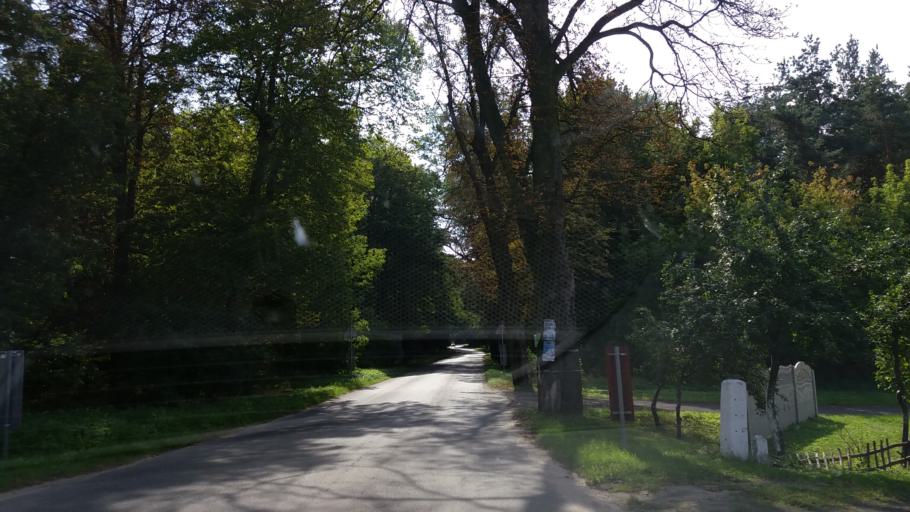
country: PL
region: West Pomeranian Voivodeship
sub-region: Powiat stargardzki
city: Stargard Szczecinski
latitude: 53.3579
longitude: 14.9724
